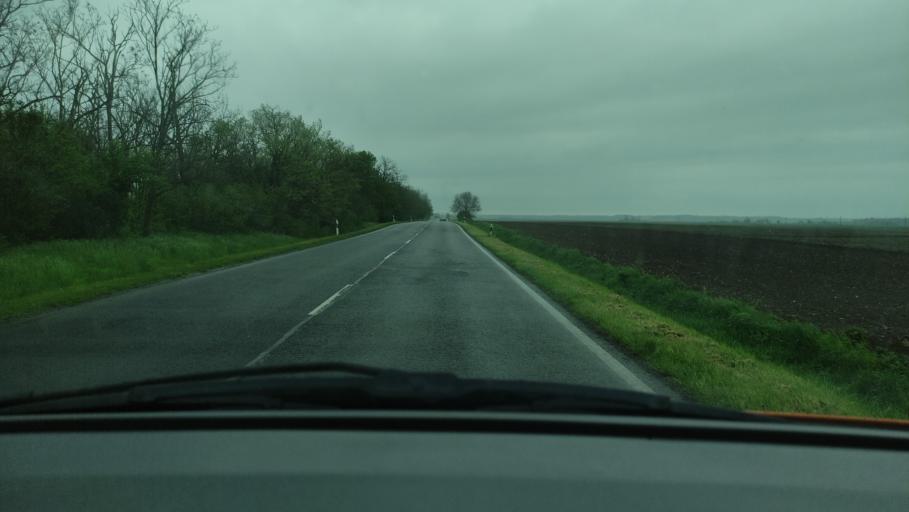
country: HU
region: Baranya
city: Mohacs
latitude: 45.9263
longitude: 18.6595
